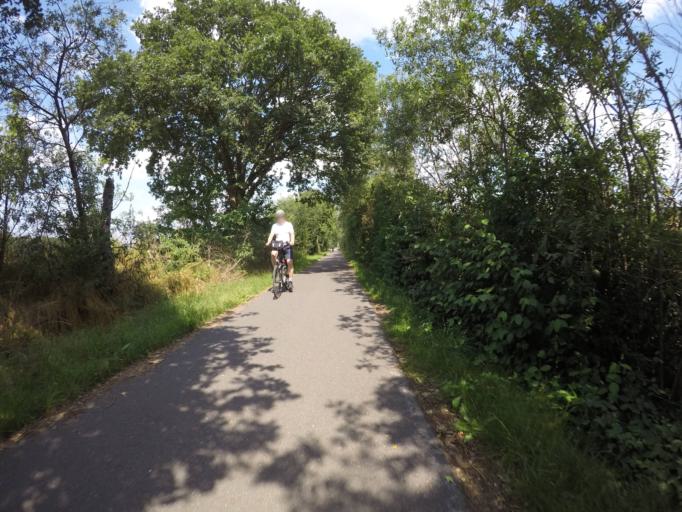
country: DE
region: North Rhine-Westphalia
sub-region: Regierungsbezirk Munster
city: Borken
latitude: 51.8407
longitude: 6.8256
